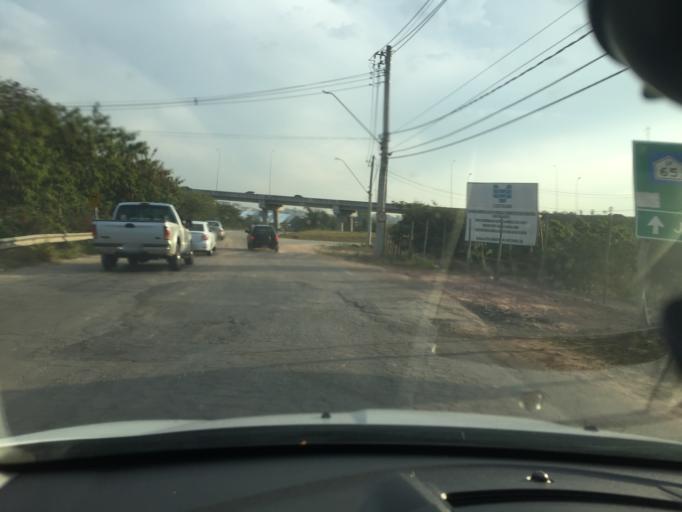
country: BR
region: Sao Paulo
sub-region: Campo Limpo Paulista
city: Campo Limpo Paulista
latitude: -23.1995
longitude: -46.7954
